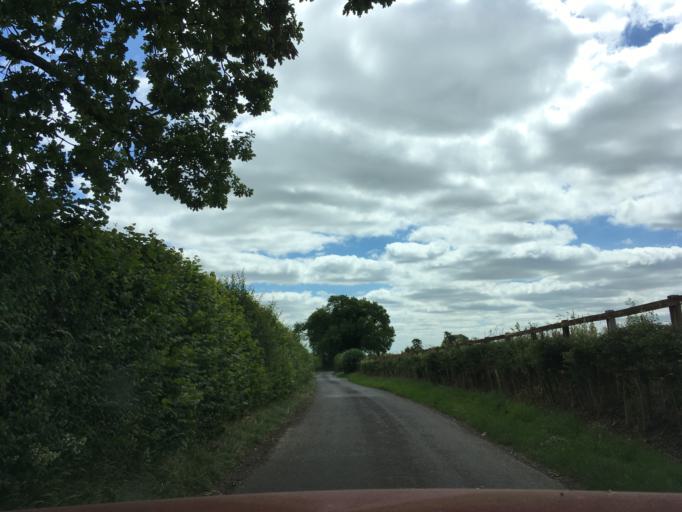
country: GB
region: England
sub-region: Hampshire
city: Highclere
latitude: 51.2725
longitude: -1.4200
